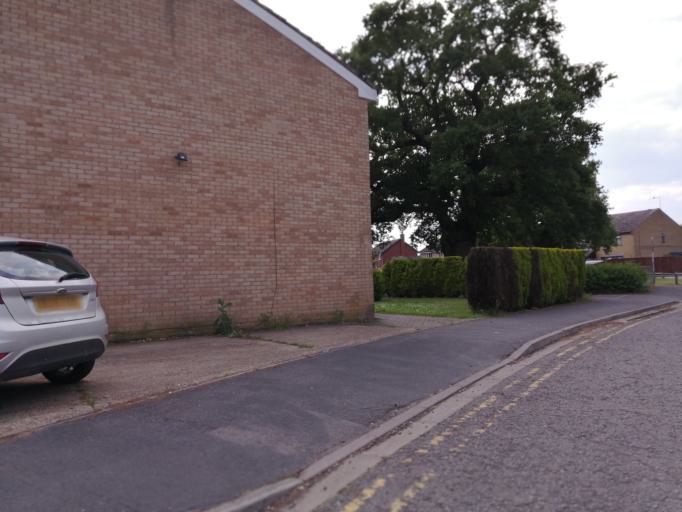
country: GB
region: England
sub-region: Peterborough
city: Marholm
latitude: 52.5764
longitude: -0.2903
